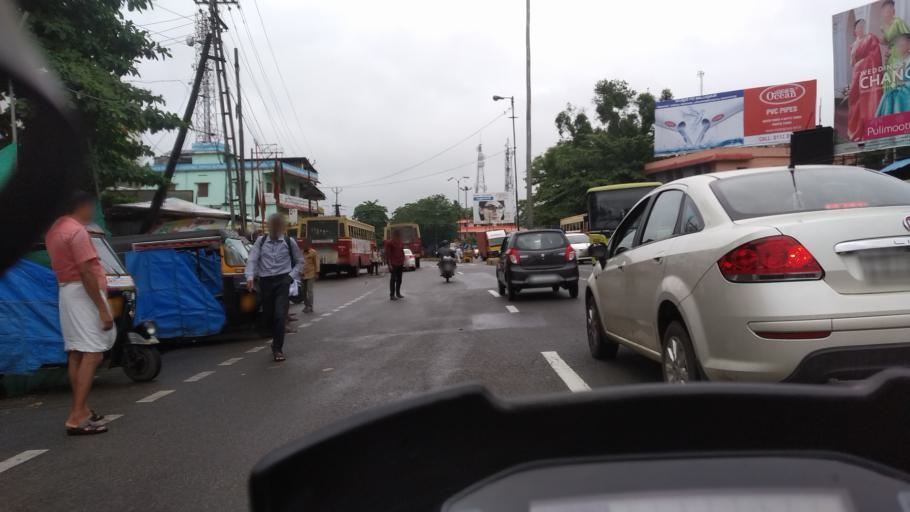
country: IN
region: Kerala
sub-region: Alappuzha
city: Mavelikara
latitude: 9.2790
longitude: 76.4595
